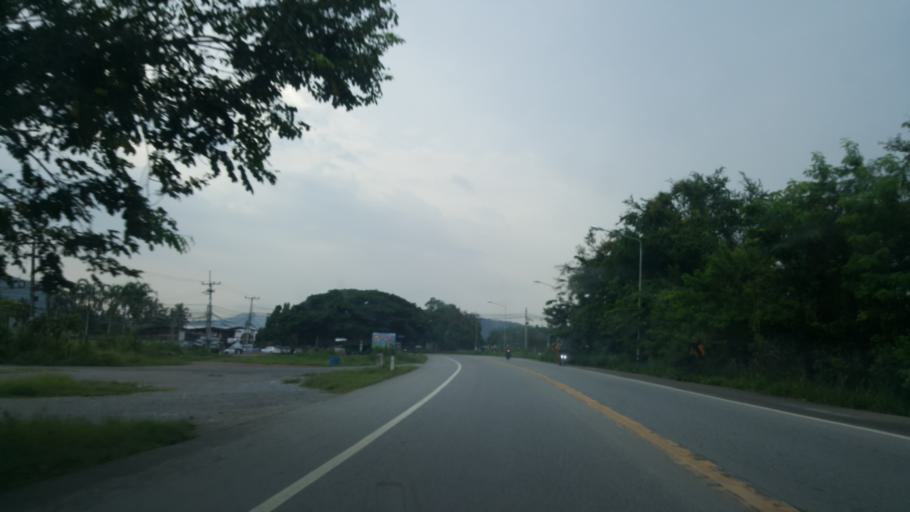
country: TH
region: Rayong
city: Ban Chang
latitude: 12.7271
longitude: 100.9794
